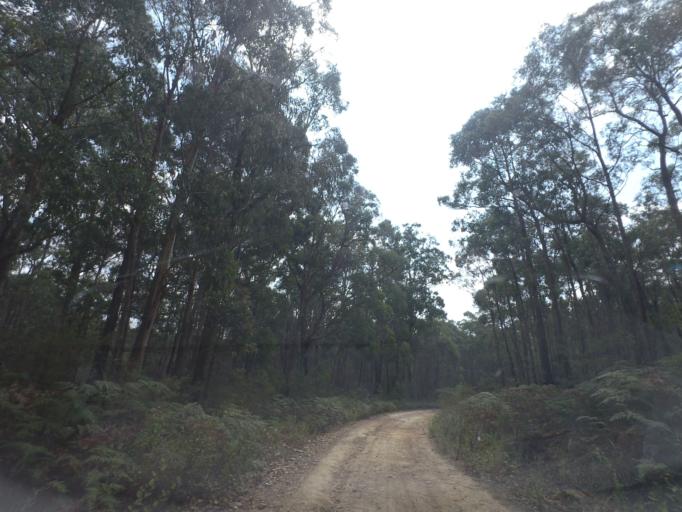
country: AU
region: Victoria
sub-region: Moorabool
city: Bacchus Marsh
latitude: -37.4620
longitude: 144.3861
